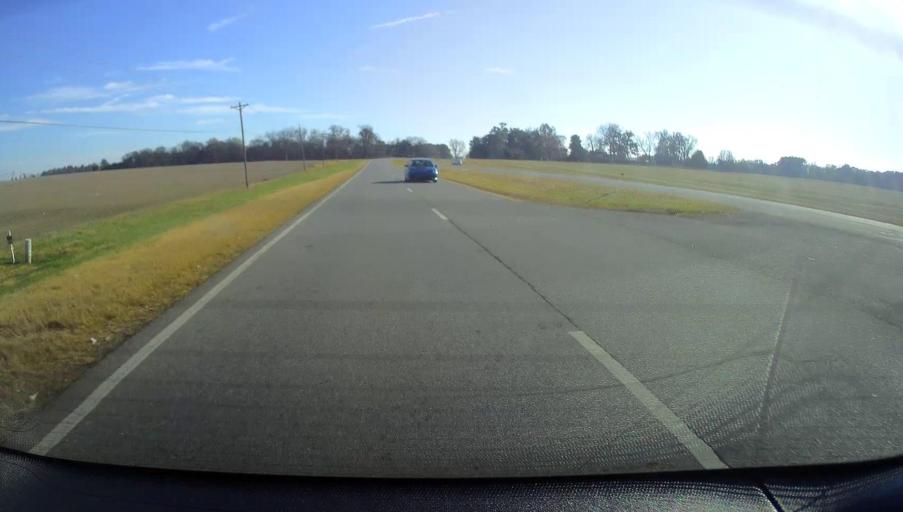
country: US
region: Alabama
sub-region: Morgan County
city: Decatur
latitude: 34.6839
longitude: -86.9509
